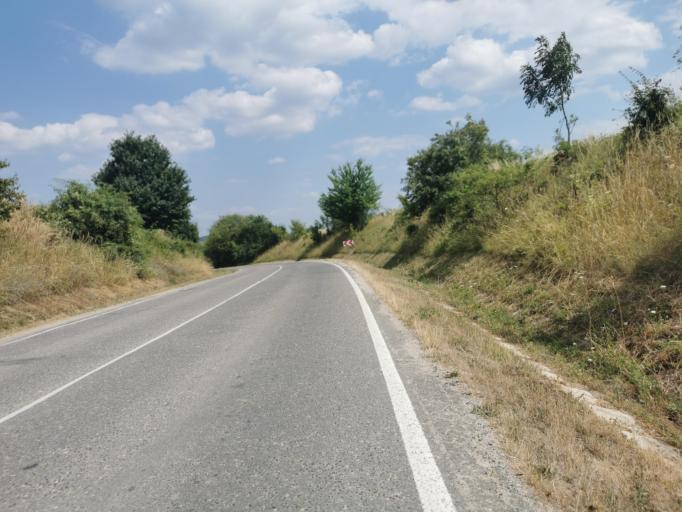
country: SK
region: Trnavsky
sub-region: Okres Senica
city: Senica
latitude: 48.6781
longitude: 17.4273
